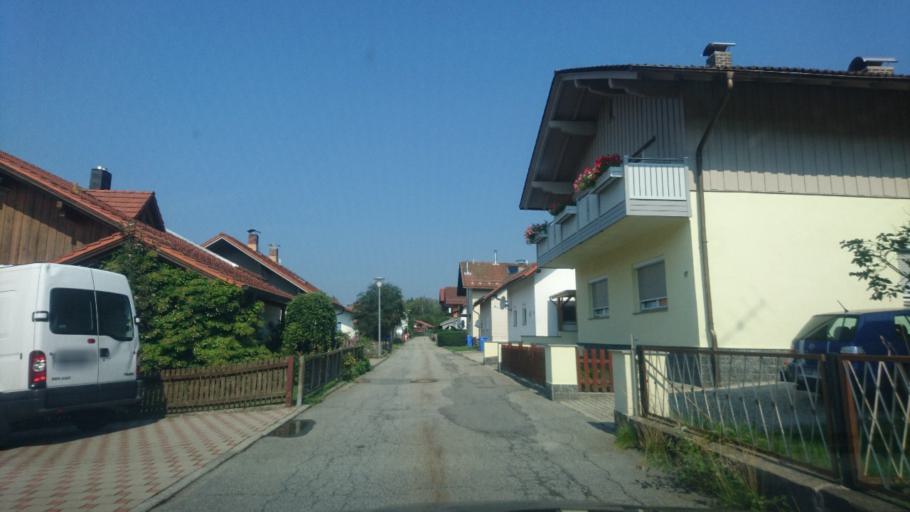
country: DE
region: Bavaria
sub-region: Lower Bavaria
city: Spiegelau
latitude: 48.9191
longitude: 13.3607
